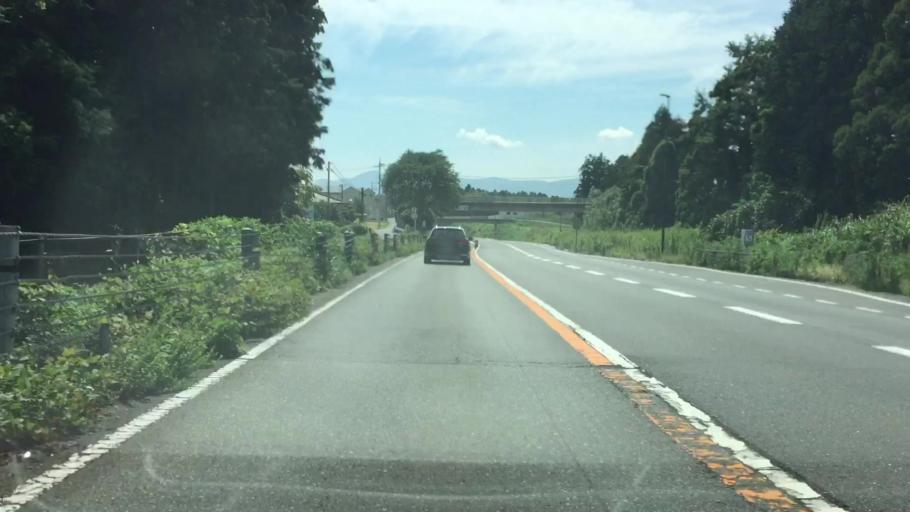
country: JP
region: Shizuoka
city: Fujinomiya
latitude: 35.2799
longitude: 138.6124
